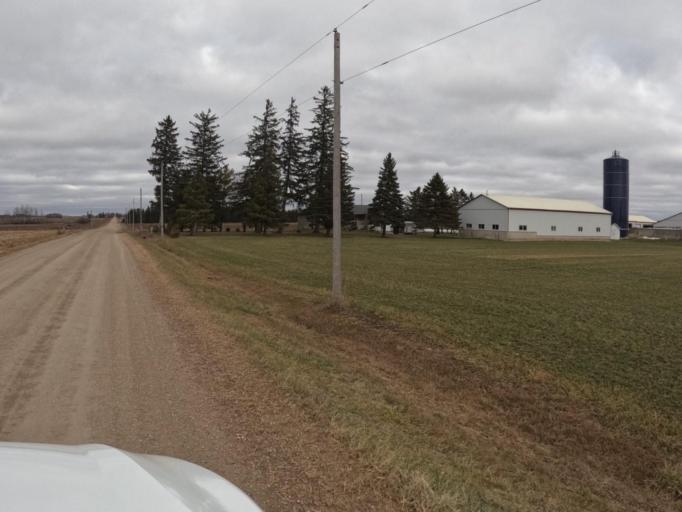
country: CA
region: Ontario
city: Shelburne
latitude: 43.8638
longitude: -80.4004
